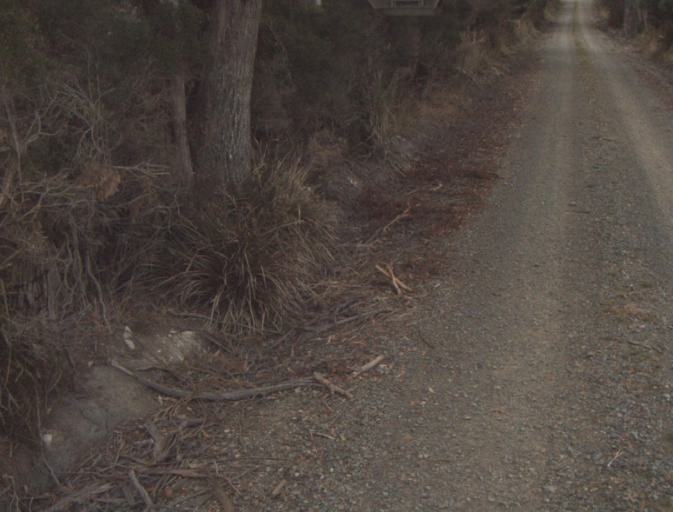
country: AU
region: Tasmania
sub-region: Launceston
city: Mayfield
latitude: -41.2416
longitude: 147.1651
